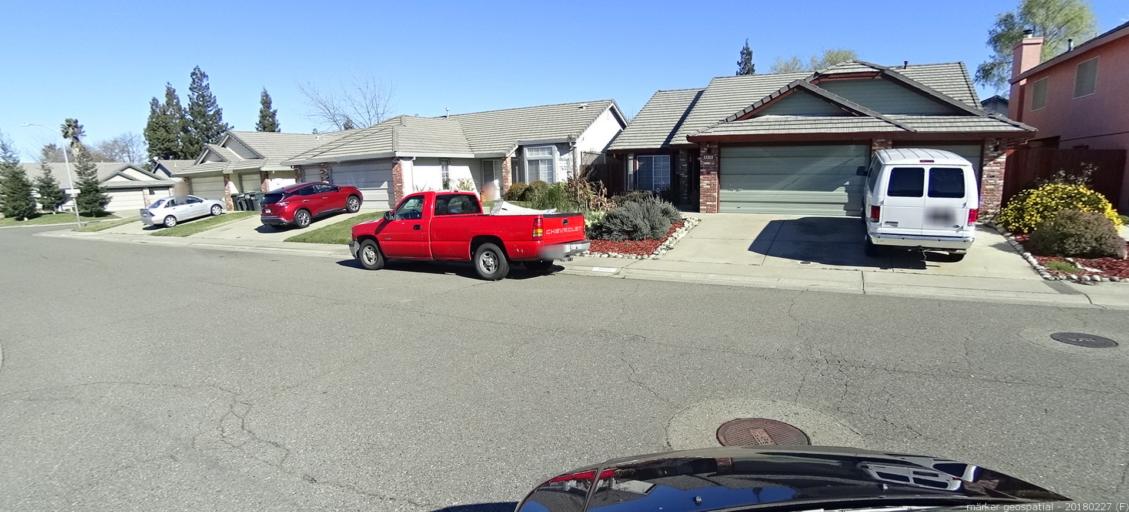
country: US
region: California
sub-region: Sacramento County
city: North Highlands
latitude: 38.7222
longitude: -121.3715
